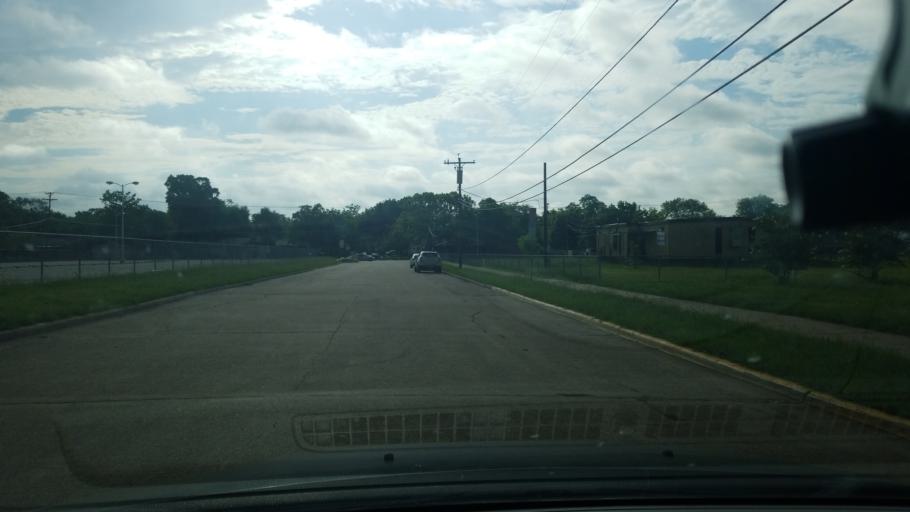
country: US
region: Texas
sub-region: Dallas County
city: Balch Springs
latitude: 32.7468
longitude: -96.6671
